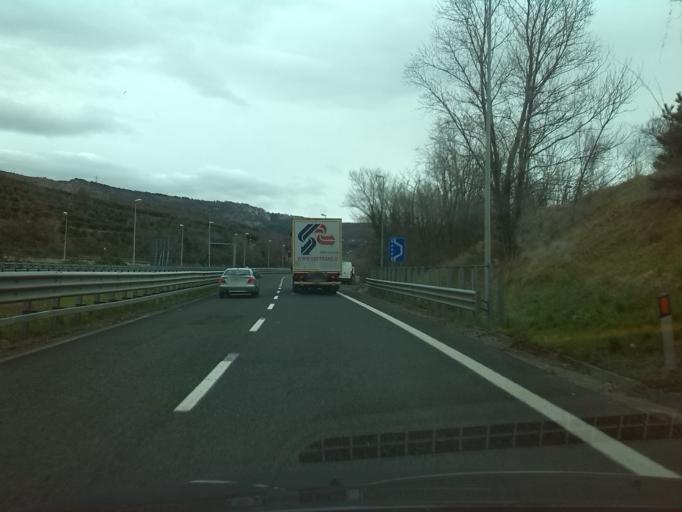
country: IT
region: Friuli Venezia Giulia
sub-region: Provincia di Trieste
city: Domio
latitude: 45.6089
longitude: 13.8397
